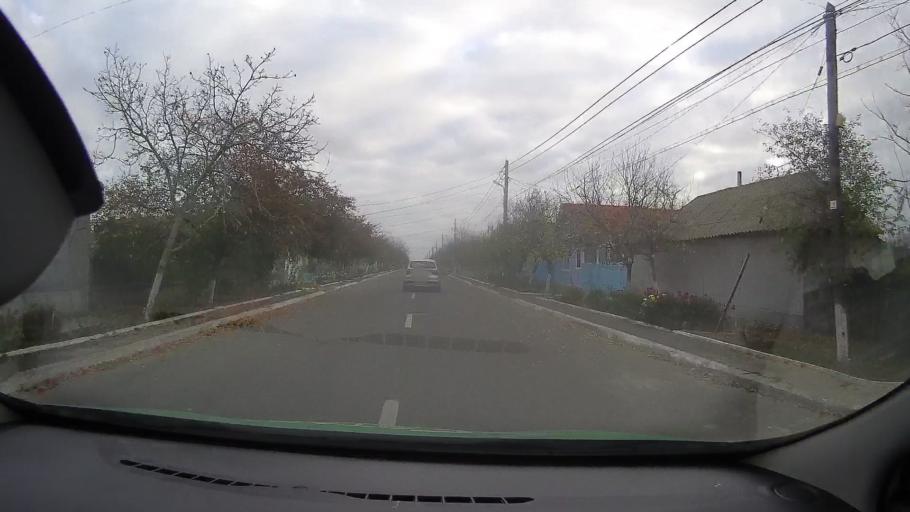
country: RO
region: Tulcea
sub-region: Comuna Jurilovca
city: Jurilovca
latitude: 44.7598
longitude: 28.8783
